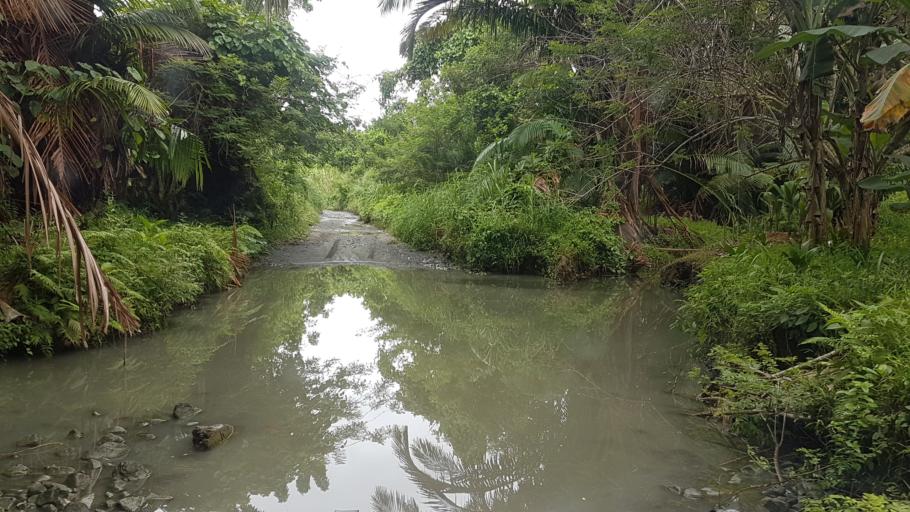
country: PG
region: East Sepik
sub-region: Wewak
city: Wewak
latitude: -3.3764
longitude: 143.1053
